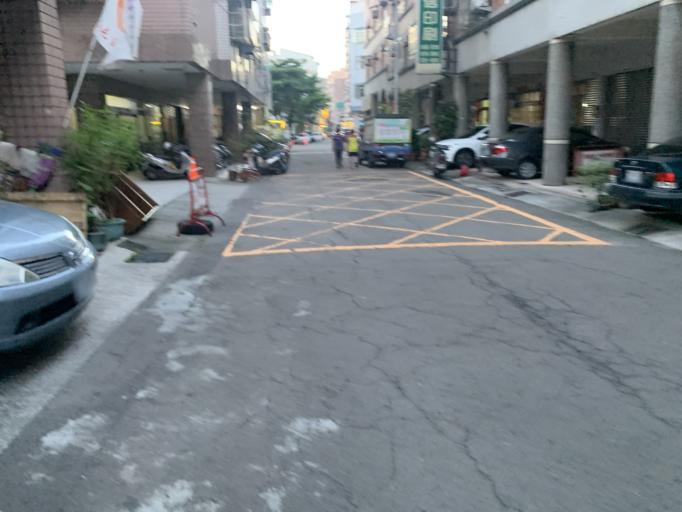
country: TW
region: Taiwan
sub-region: Taichung City
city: Taichung
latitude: 24.1509
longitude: 120.6142
